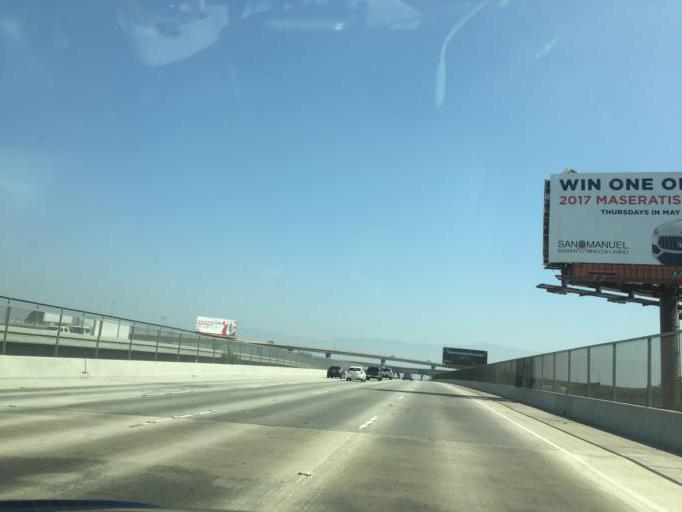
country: US
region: California
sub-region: San Bernardino County
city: Colton
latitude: 34.0593
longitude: -117.2973
